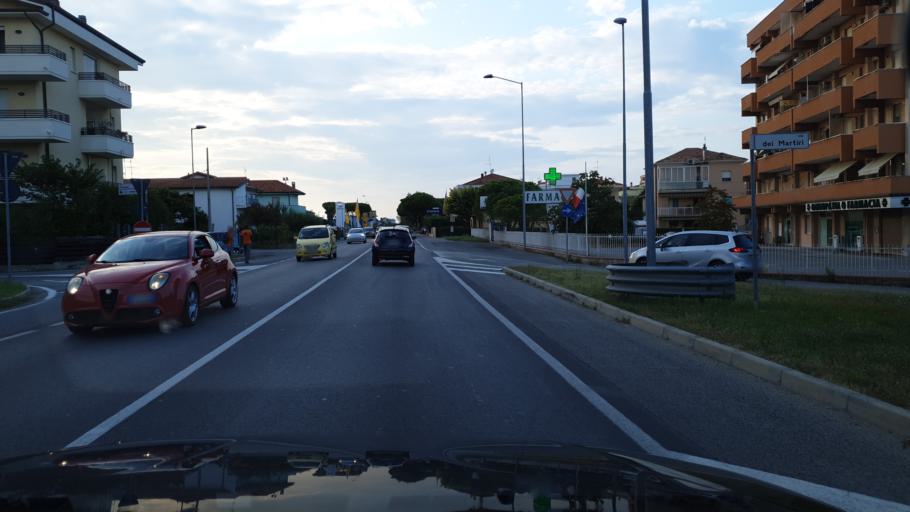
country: IT
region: Emilia-Romagna
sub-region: Provincia di Rimini
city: Rivazzurra
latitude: 44.0335
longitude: 12.6036
